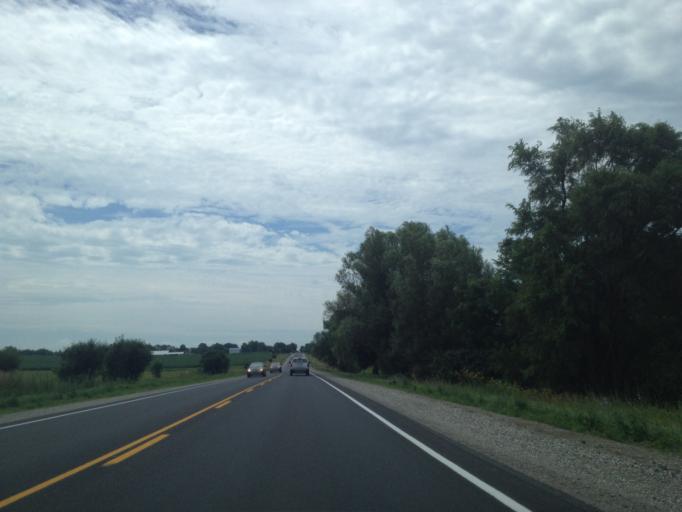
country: CA
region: Ontario
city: Ingersoll
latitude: 43.0080
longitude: -80.8336
